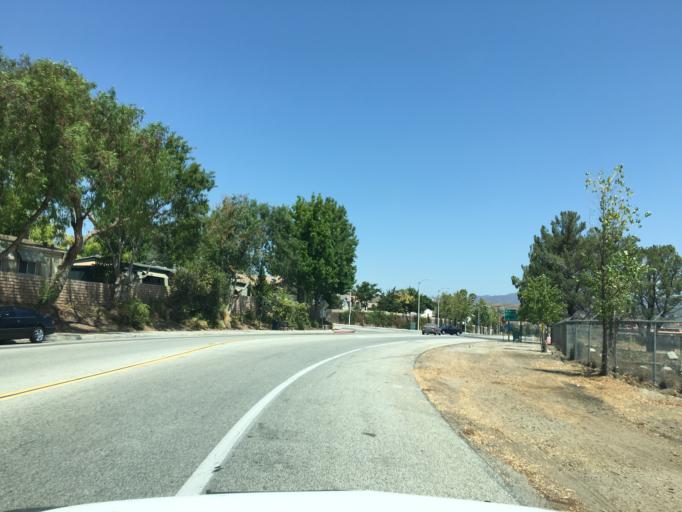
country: US
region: California
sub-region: Los Angeles County
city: Castaic
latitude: 34.4883
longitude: -118.6211
